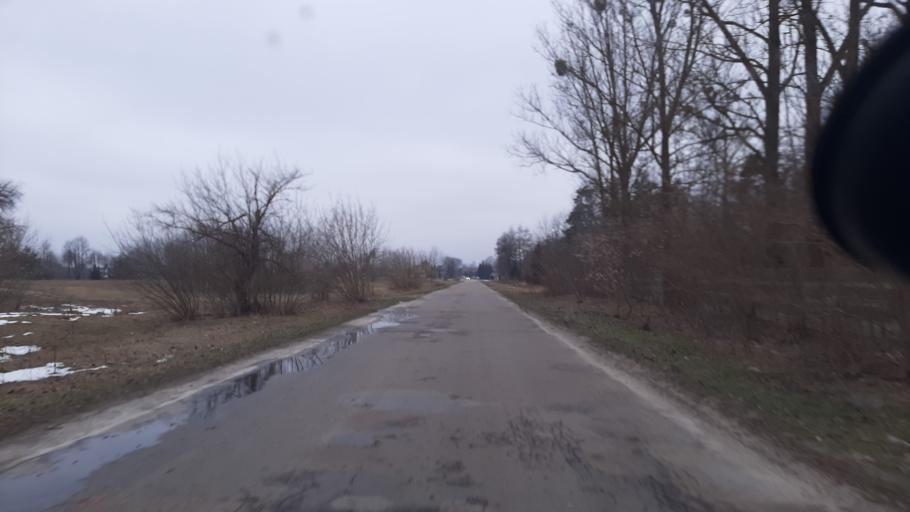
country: PL
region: Lublin Voivodeship
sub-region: Powiat wlodawski
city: Wlodawa
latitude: 51.5206
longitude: 23.5845
